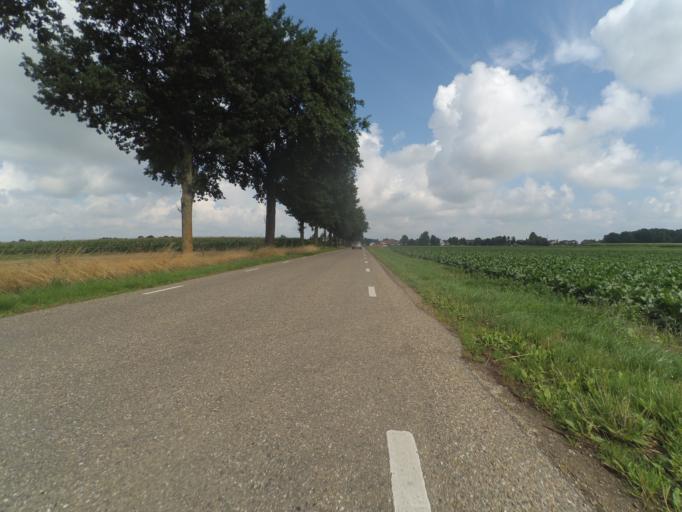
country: NL
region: Limburg
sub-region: Gemeente Echt-Susteren
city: Koningsbosch
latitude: 51.0470
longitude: 5.9478
